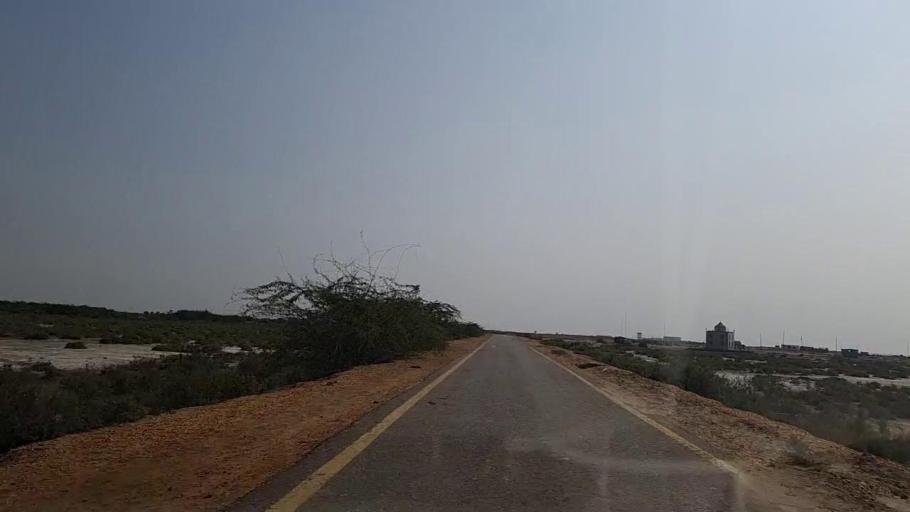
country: PK
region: Sindh
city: Chuhar Jamali
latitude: 24.1714
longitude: 67.8934
